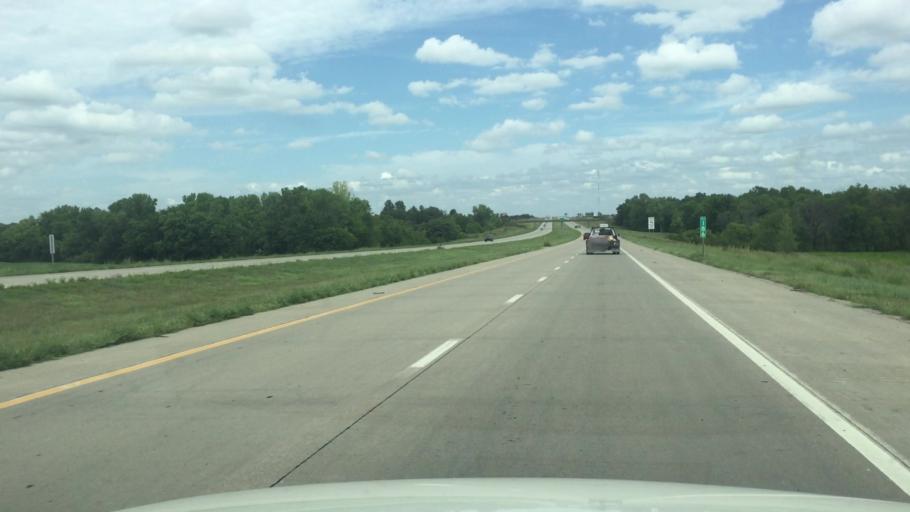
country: US
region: Kansas
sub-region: Franklin County
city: Ottawa
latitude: 38.6019
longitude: -95.2328
